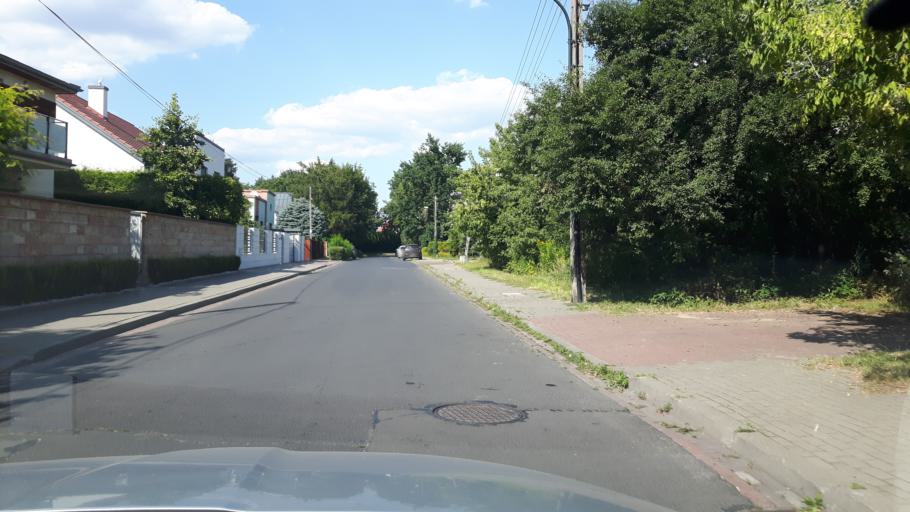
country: PL
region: Masovian Voivodeship
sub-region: Warszawa
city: Wlochy
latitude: 52.2078
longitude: 20.9300
